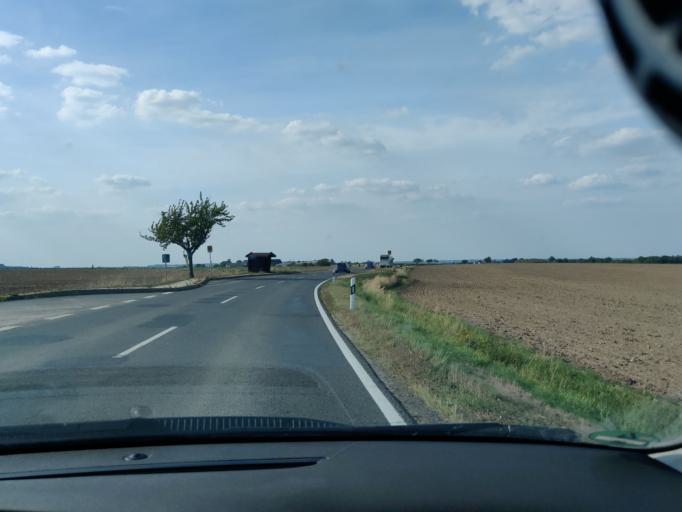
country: DE
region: Saxony
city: Seelitz
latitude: 51.0261
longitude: 12.8440
